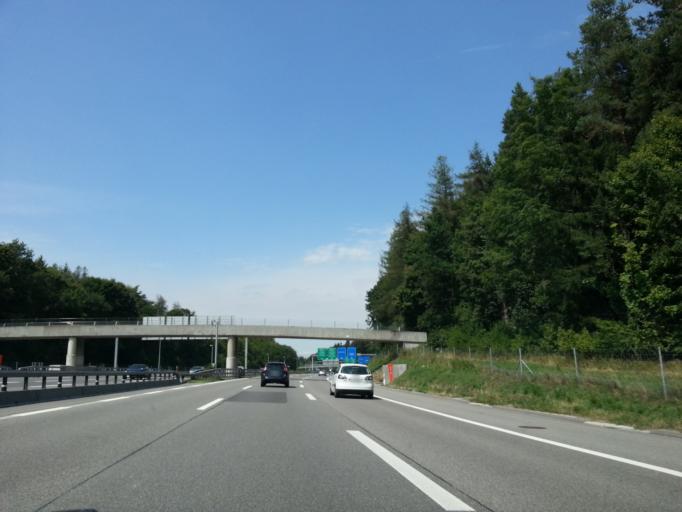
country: CH
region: Bern
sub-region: Bern-Mittelland District
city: Koniz
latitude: 46.9516
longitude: 7.4002
